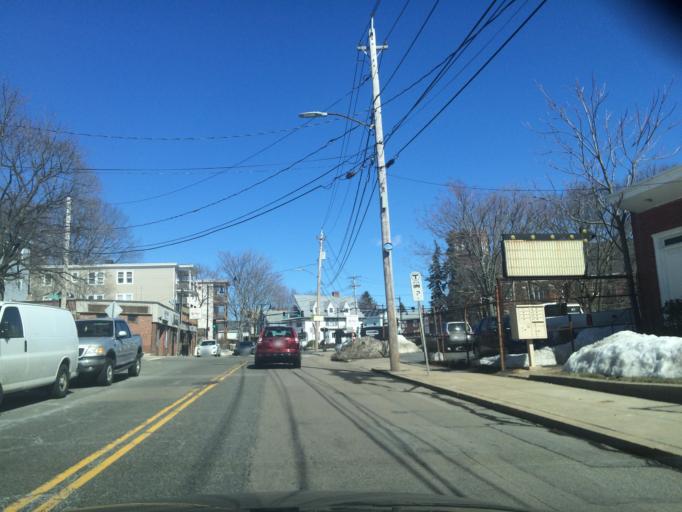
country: US
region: Massachusetts
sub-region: Norfolk County
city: Dedham
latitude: 42.2512
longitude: -71.1310
